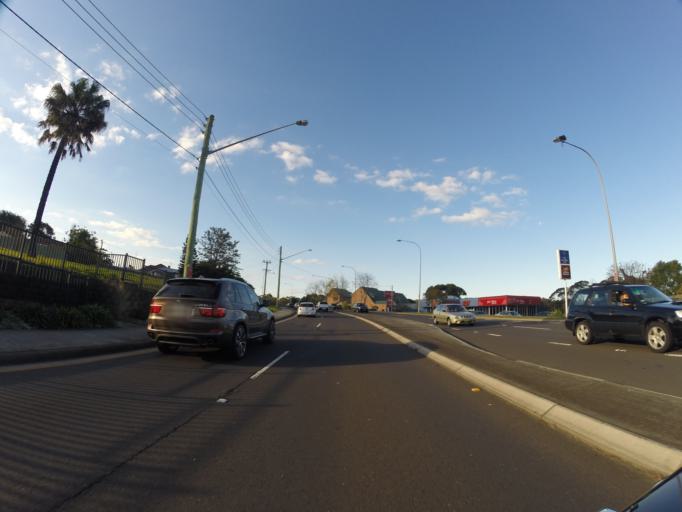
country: AU
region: New South Wales
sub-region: Wollongong
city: Mangerton
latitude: -34.4383
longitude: 150.8589
